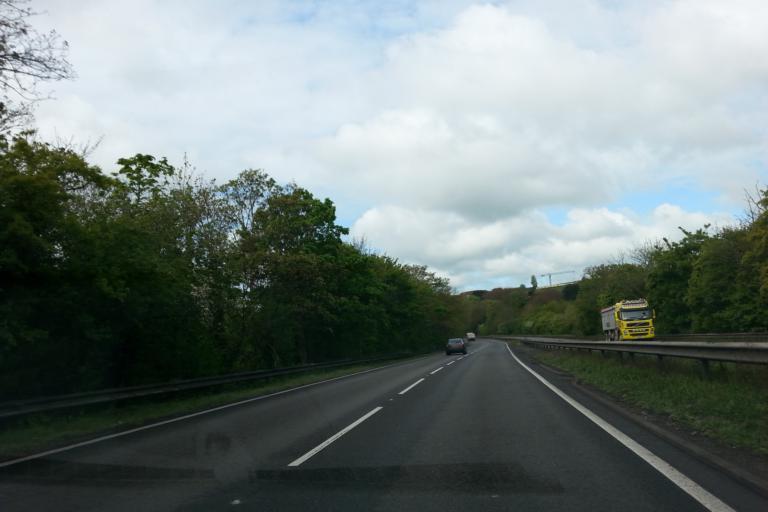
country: GB
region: England
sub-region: Staffordshire
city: Burton upon Trent
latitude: 52.8153
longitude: -1.6493
